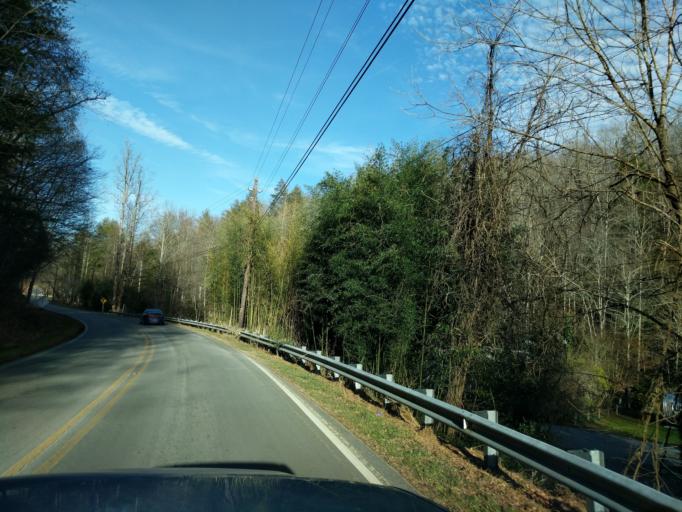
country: US
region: North Carolina
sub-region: Henderson County
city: Edneyville
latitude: 35.4026
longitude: -82.3237
